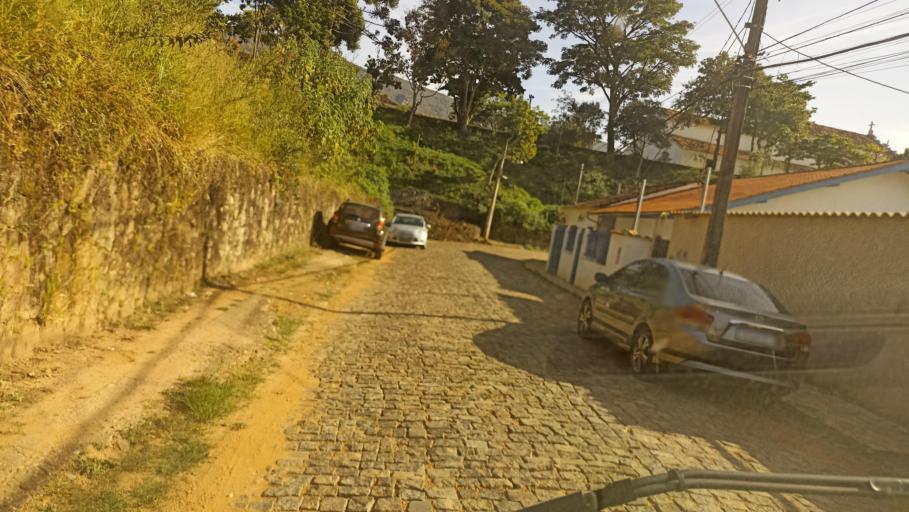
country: BR
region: Minas Gerais
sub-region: Tiradentes
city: Tiradentes
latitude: -21.1139
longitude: -44.1833
